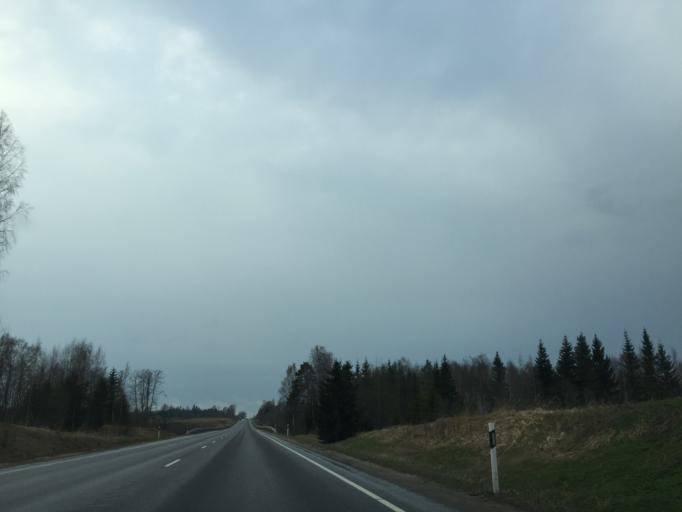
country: EE
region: Tartu
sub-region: UElenurme vald
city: Ulenurme
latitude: 58.1353
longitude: 26.7171
